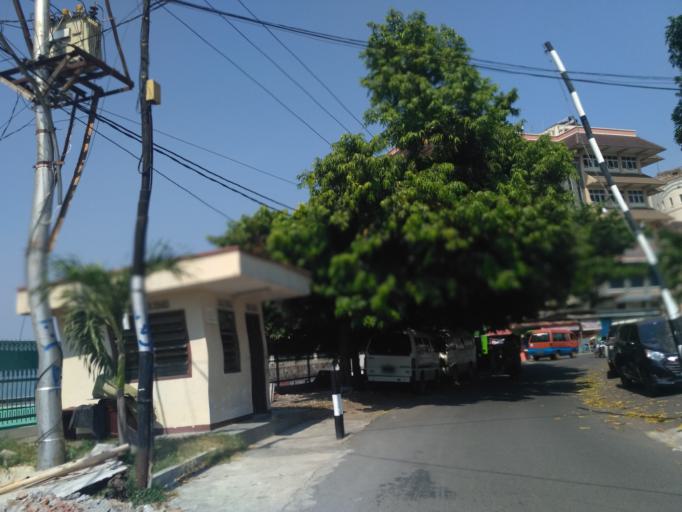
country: ID
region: Central Java
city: Semarang
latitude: -7.0061
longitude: 110.4207
